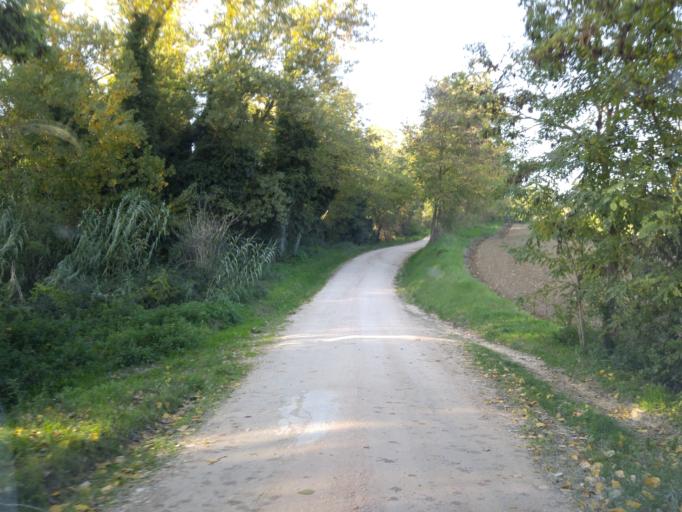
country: IT
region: The Marches
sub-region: Provincia di Pesaro e Urbino
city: Montefelcino
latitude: 43.7233
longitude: 12.8326
